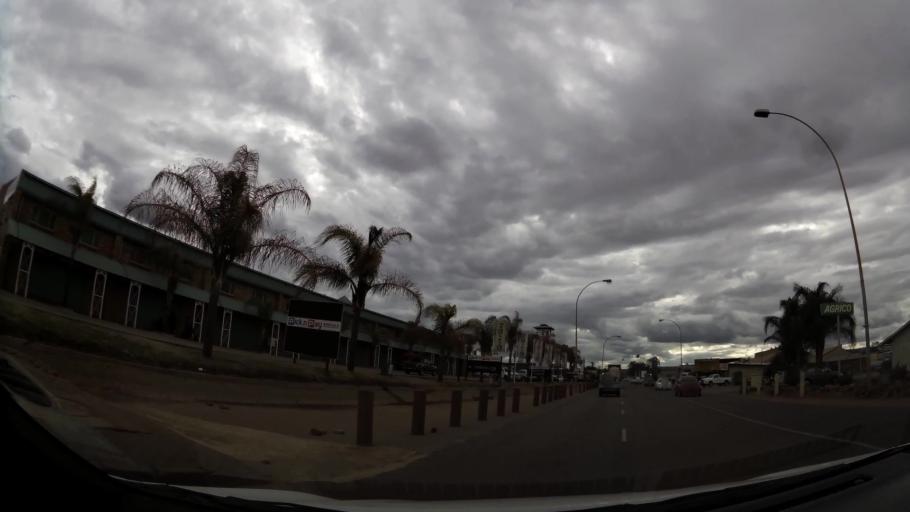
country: ZA
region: Limpopo
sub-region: Waterberg District Municipality
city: Modimolle
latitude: -24.7116
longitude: 28.4164
